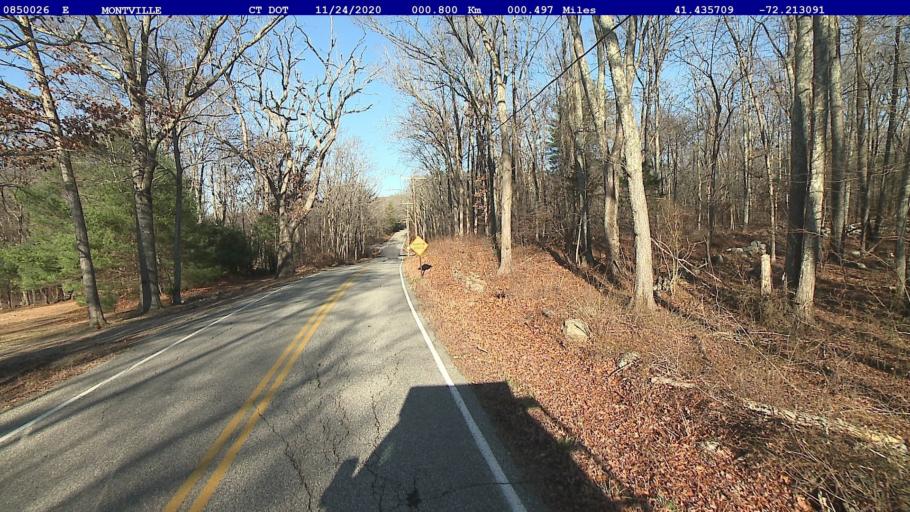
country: US
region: Connecticut
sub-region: New London County
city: Montville Center
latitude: 41.4357
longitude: -72.2131
